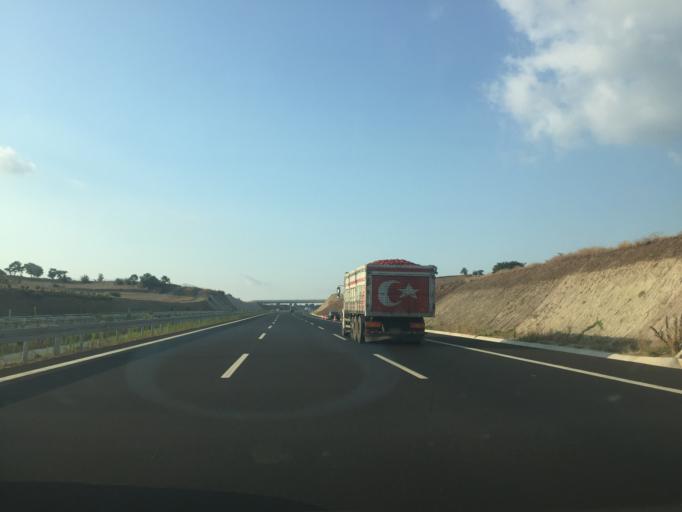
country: TR
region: Balikesir
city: Ertugrul
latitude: 39.6055
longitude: 27.7027
